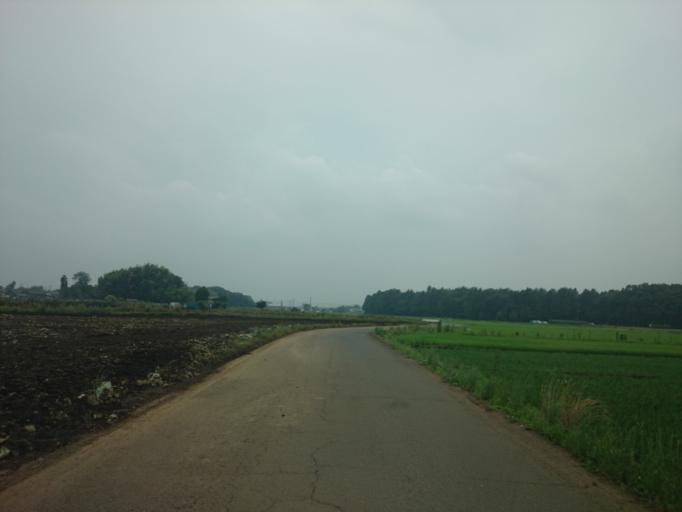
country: JP
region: Ibaraki
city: Tsukuba
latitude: 36.1099
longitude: 140.0695
